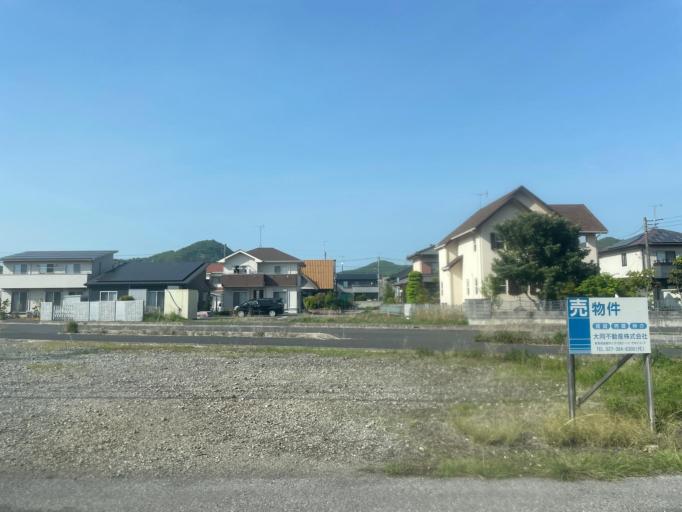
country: JP
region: Tochigi
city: Ashikaga
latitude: 36.3175
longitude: 139.4969
